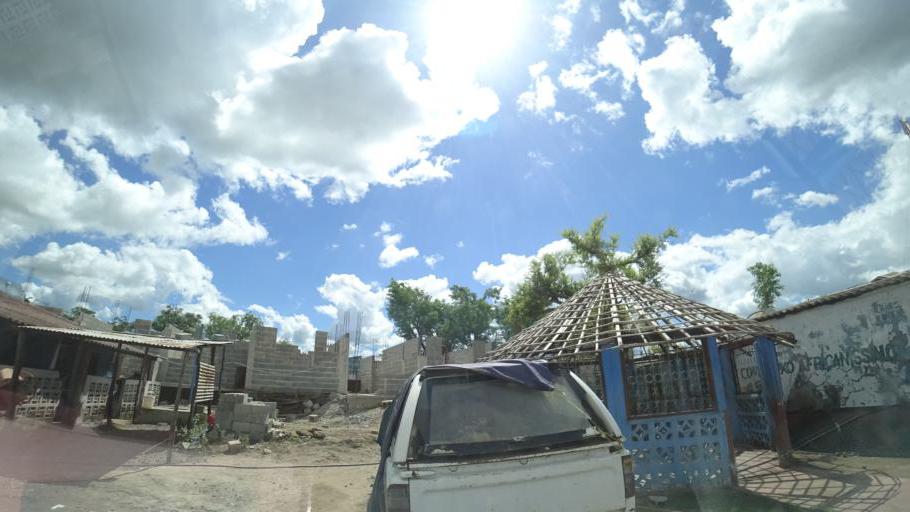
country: MZ
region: Sofala
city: Dondo
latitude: -19.2729
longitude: 34.2038
